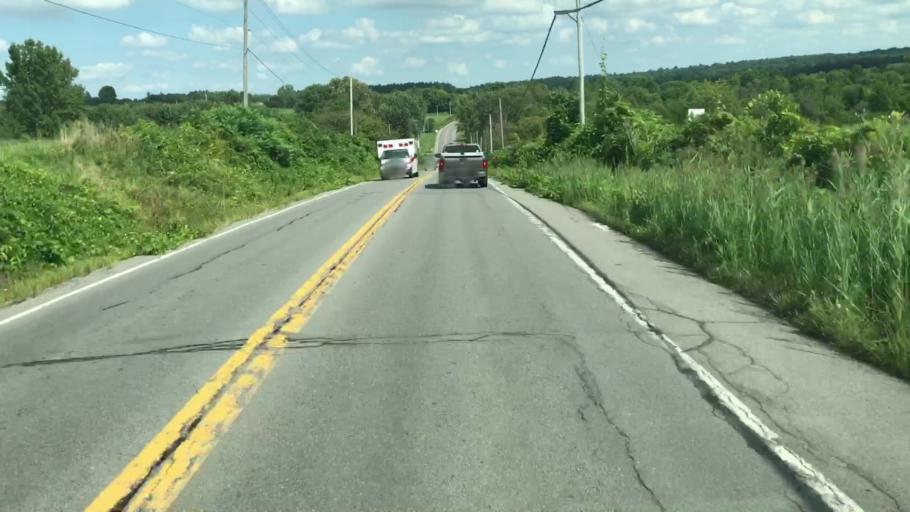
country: US
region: New York
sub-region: Onondaga County
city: Fairmount
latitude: 42.9870
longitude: -76.2594
